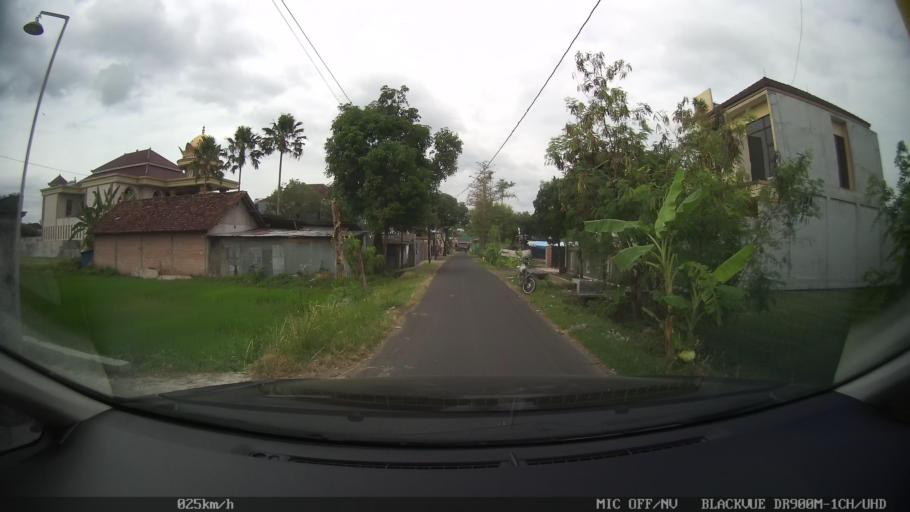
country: ID
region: Daerah Istimewa Yogyakarta
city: Depok
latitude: -7.8186
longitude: 110.4205
